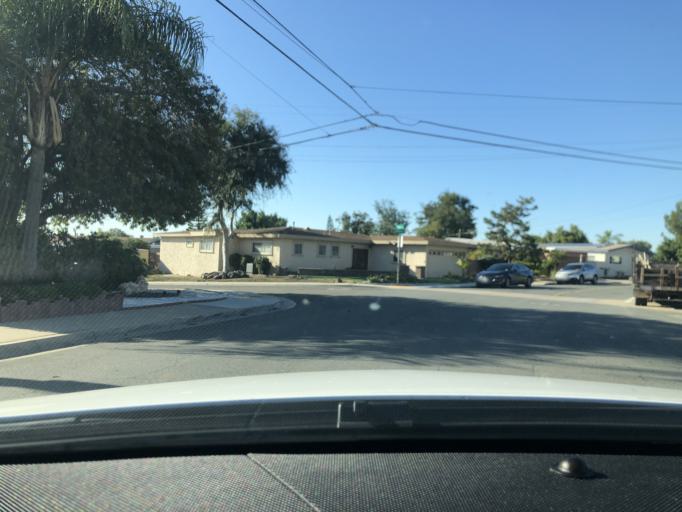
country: US
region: California
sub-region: San Diego County
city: Lemon Grove
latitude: 32.7517
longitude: -117.0708
